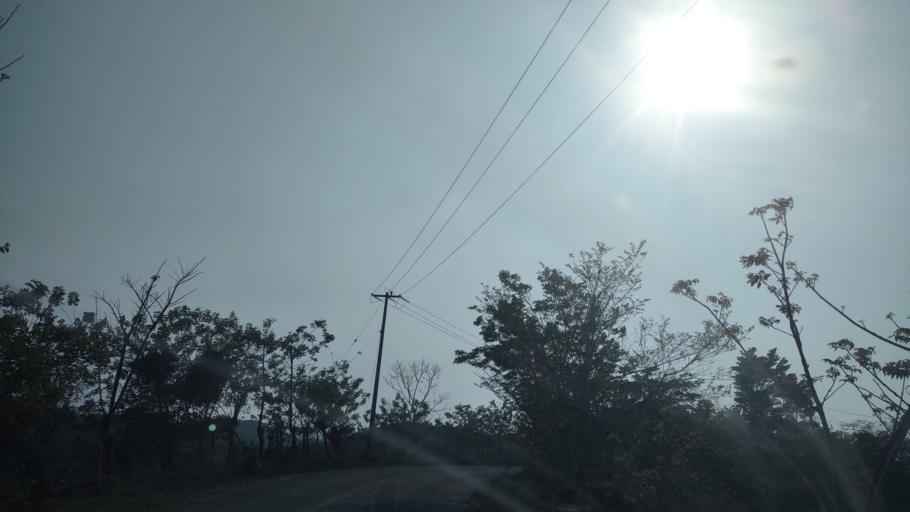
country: MX
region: Tabasco
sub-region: Huimanguillo
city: Francisco Rueda
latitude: 17.6425
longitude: -93.9124
